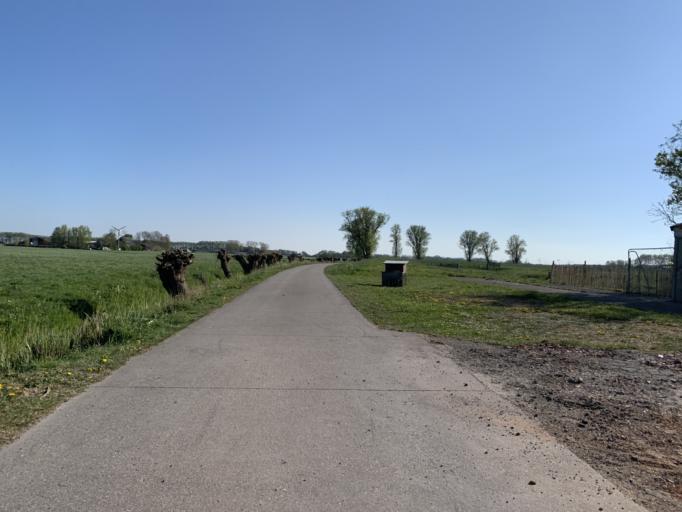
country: NL
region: Groningen
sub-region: Gemeente Winsum
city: Winsum
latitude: 53.2860
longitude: 6.5159
